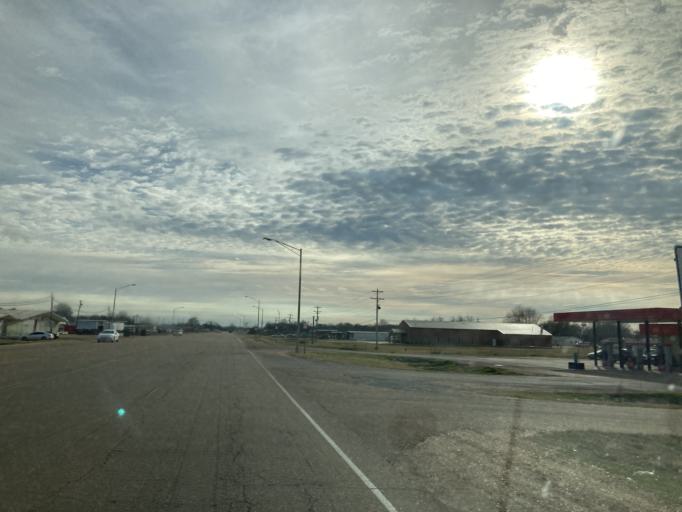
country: US
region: Mississippi
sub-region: Humphreys County
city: Belzoni
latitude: 33.1718
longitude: -90.4983
